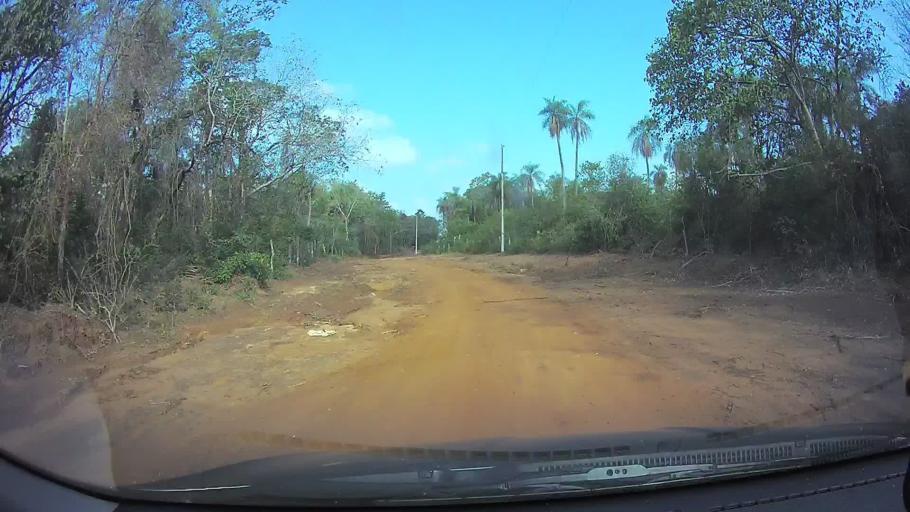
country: PY
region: Cordillera
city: Arroyos y Esteros
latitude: -25.0148
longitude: -57.1977
